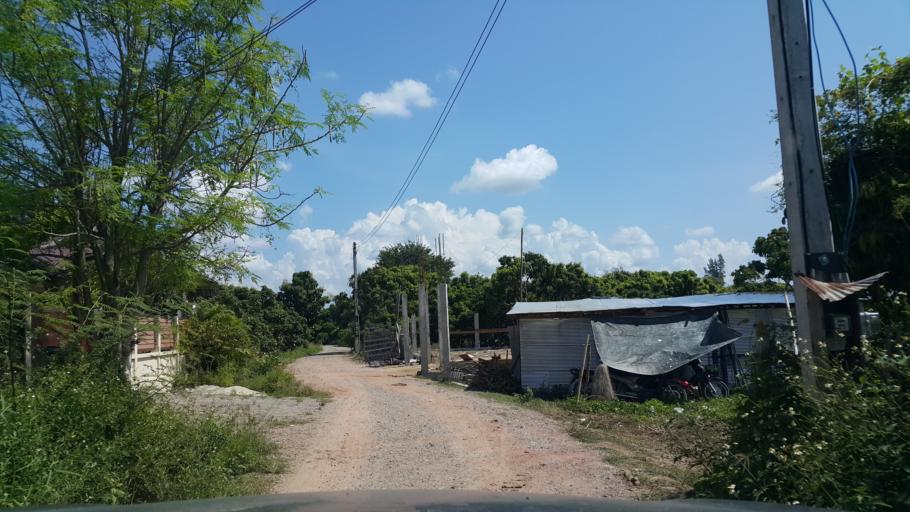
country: TH
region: Chiang Mai
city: Chom Thong
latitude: 18.4177
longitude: 98.6835
